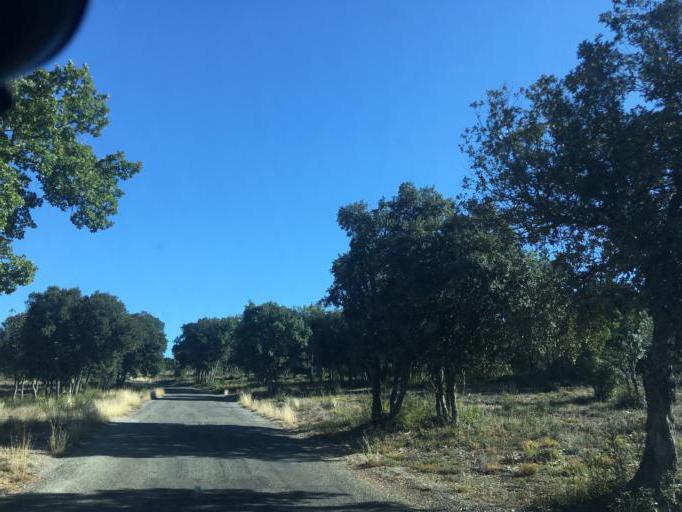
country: FR
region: Provence-Alpes-Cote d'Azur
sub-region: Departement des Alpes-de-Haute-Provence
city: Riez
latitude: 43.7422
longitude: 6.0980
